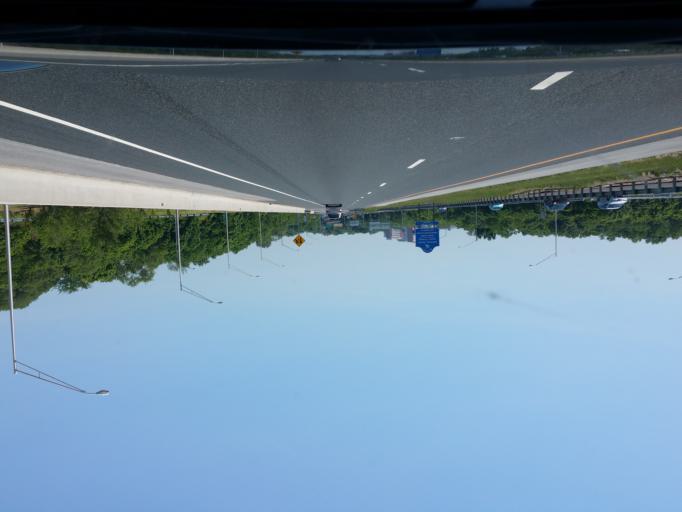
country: US
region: Maryland
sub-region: Baltimore County
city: Rosedale
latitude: 39.3105
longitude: -76.5413
